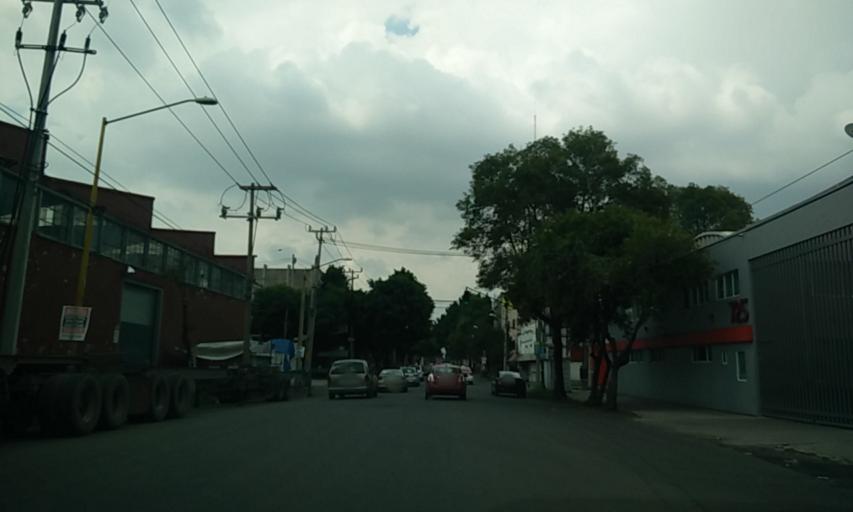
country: MX
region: Mexico City
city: Azcapotzalco
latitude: 19.4831
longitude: -99.1568
